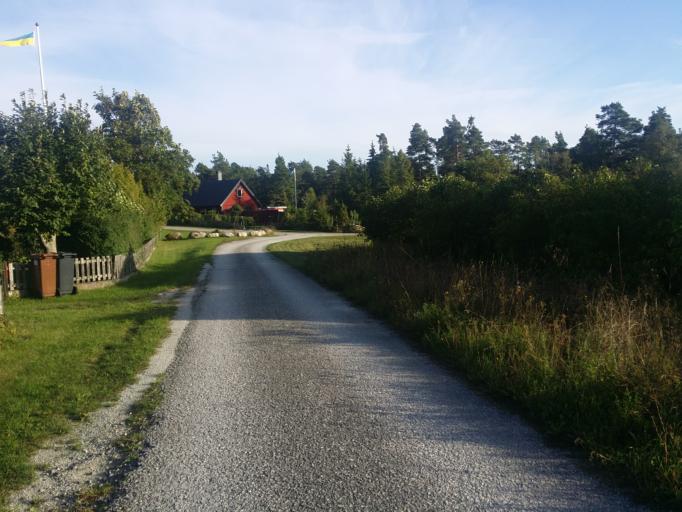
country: SE
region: Gotland
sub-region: Gotland
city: Klintehamn
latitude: 57.4832
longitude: 18.1376
